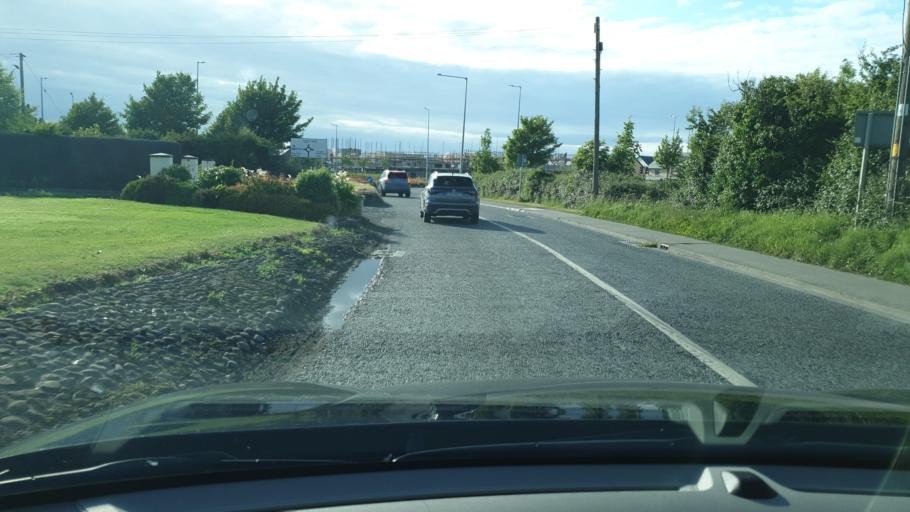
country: IE
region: Leinster
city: Lusk
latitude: 53.5231
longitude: -6.1564
